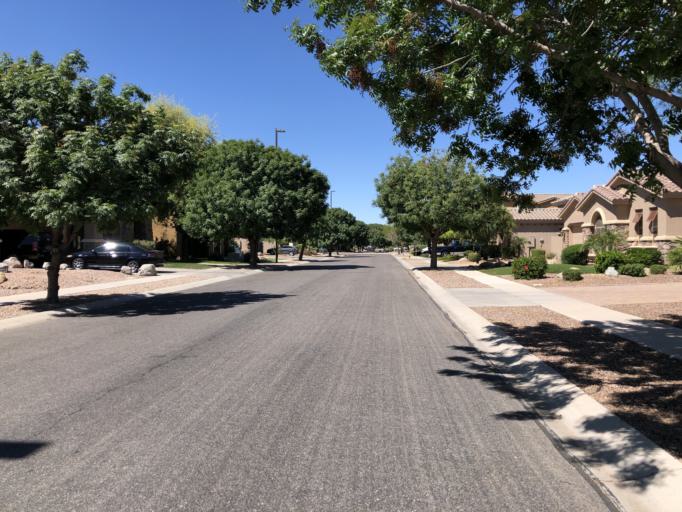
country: US
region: Arizona
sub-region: Maricopa County
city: Queen Creek
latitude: 33.2828
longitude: -111.6970
